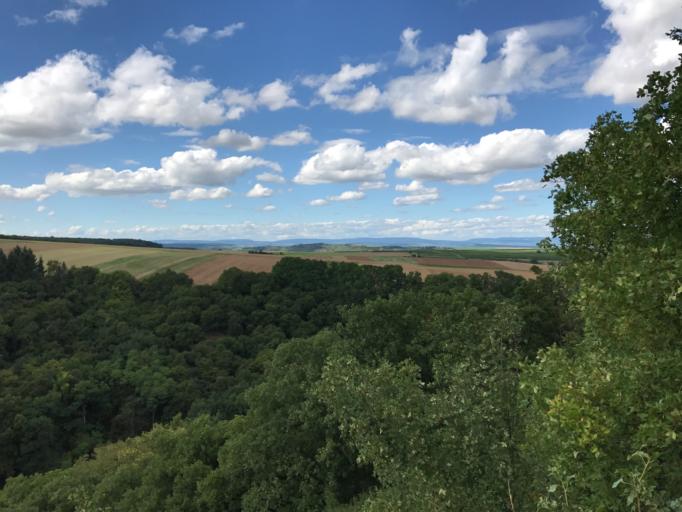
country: DE
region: Rheinland-Pfalz
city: Nieder-Wiesen
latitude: 49.7487
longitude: 7.9792
